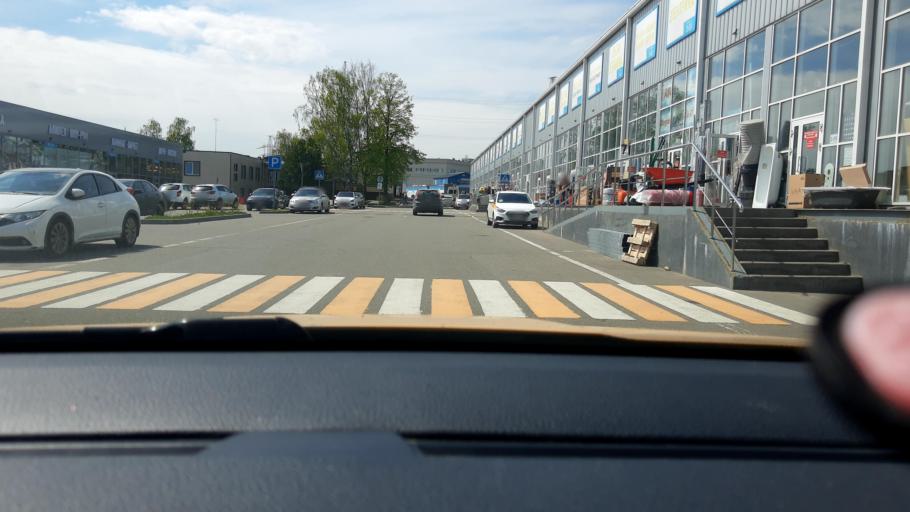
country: RU
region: Moscow
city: Vatutino
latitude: 55.9007
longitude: 37.6795
